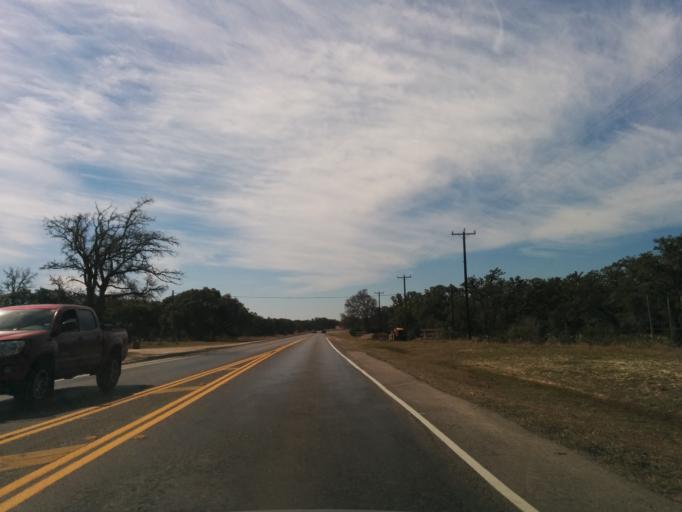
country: US
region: Texas
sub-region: Bexar County
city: Fair Oaks Ranch
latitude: 29.7599
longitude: -98.6139
